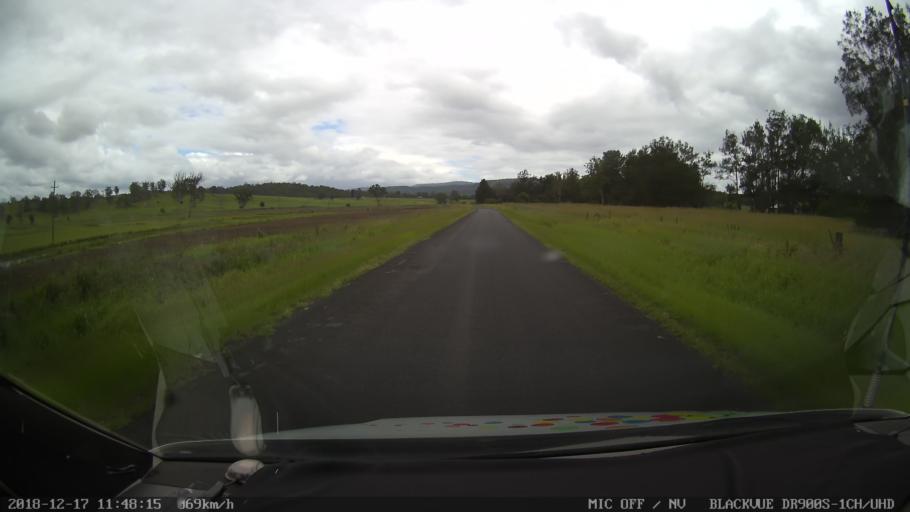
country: AU
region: New South Wales
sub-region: Kyogle
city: Kyogle
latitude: -28.6191
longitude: 152.5904
